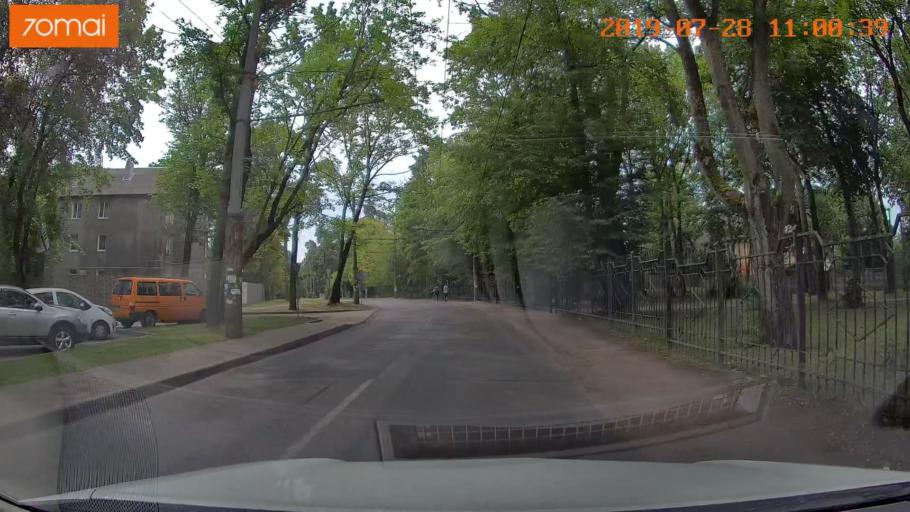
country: RU
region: Kaliningrad
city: Vzmorye
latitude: 54.7261
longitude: 20.3629
